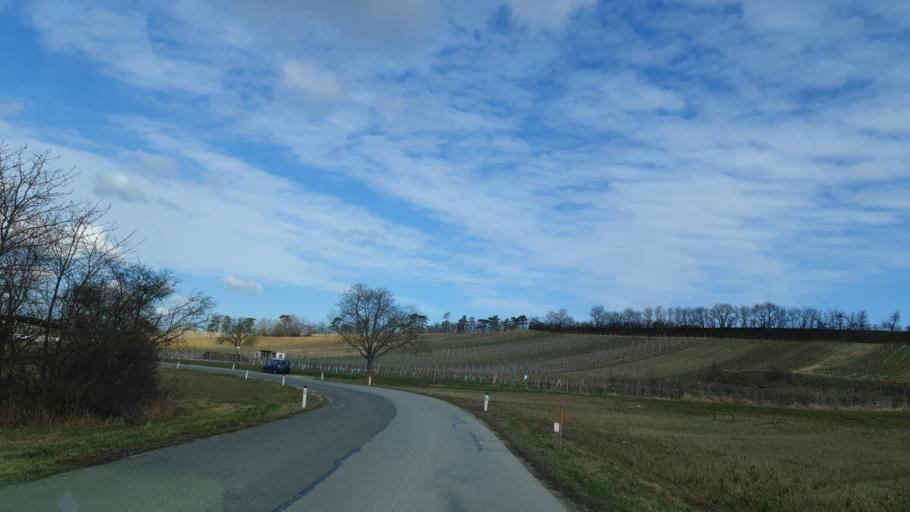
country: AT
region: Lower Austria
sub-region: Politischer Bezirk Mistelbach
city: Wolkersdorf im Weinviertel
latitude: 48.3778
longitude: 16.5300
